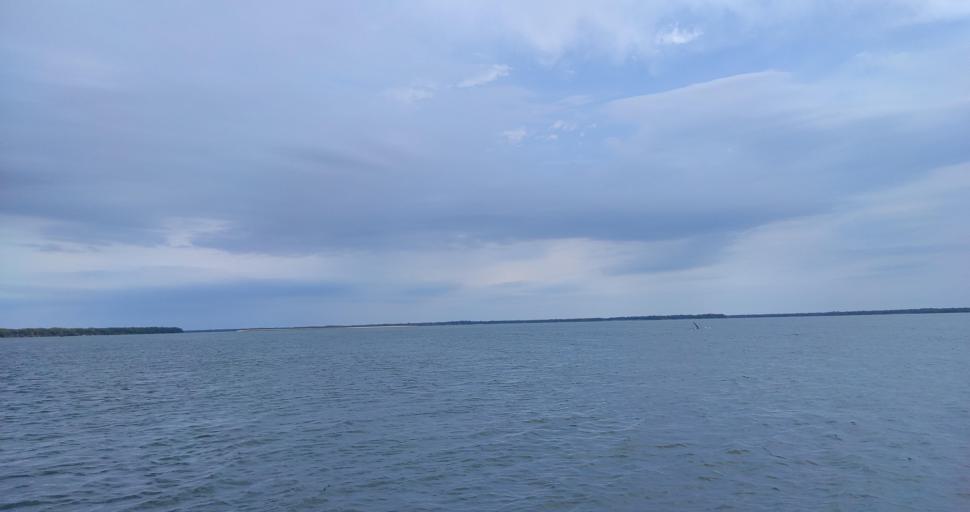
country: PY
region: Neembucu
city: Cerrito
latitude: -27.3462
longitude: -57.6867
